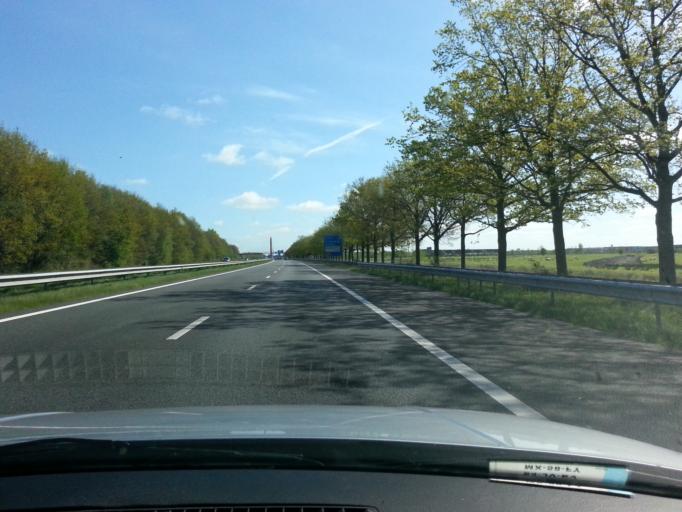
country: NL
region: Friesland
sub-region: Gemeente Smallingerland
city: Drachten
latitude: 53.0983
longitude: 6.1164
